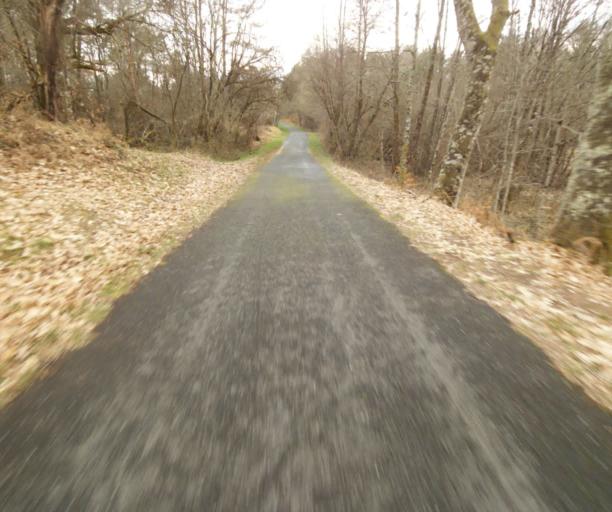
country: FR
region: Limousin
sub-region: Departement de la Correze
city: Saint-Privat
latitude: 45.2147
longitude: 2.0091
